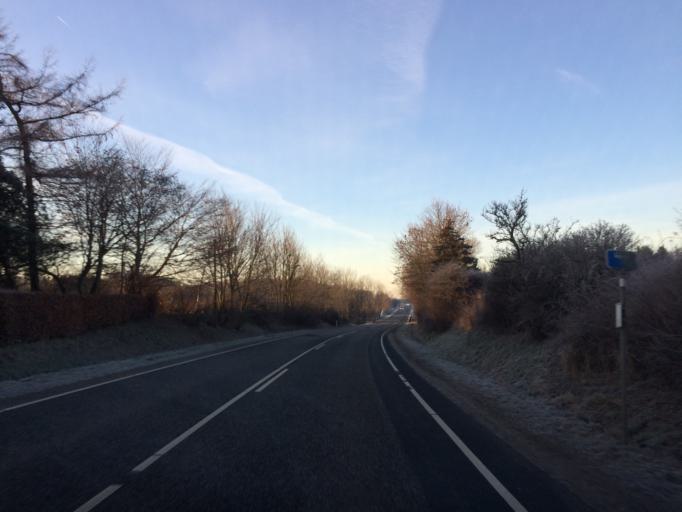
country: DK
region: South Denmark
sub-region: Odense Kommune
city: Bellinge
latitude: 55.3069
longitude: 10.3060
